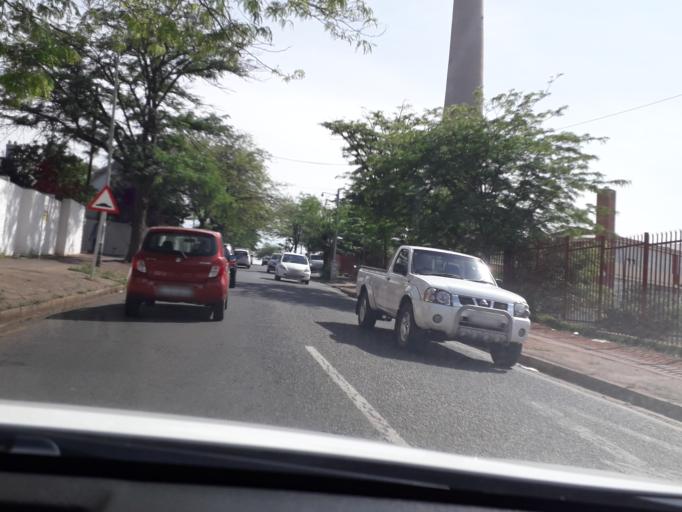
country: ZA
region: Gauteng
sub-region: City of Johannesburg Metropolitan Municipality
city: Johannesburg
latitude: -26.1940
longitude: 28.0053
